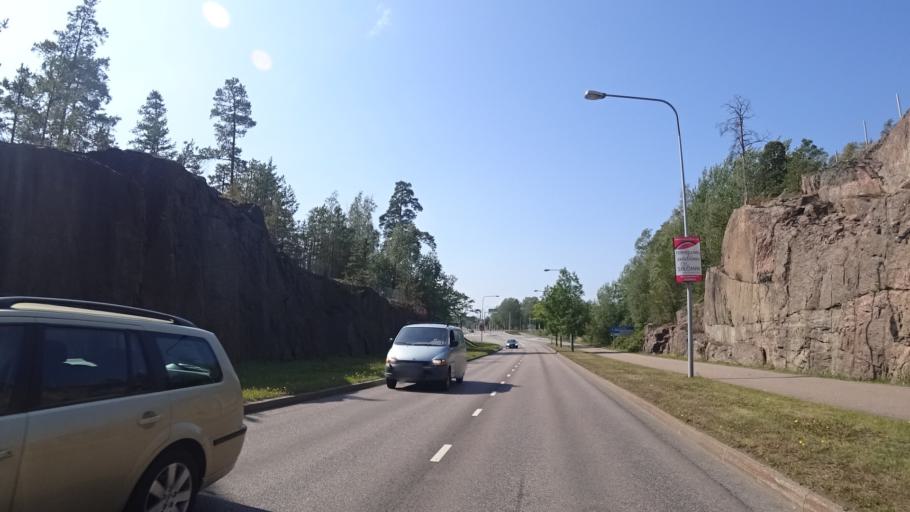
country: FI
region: Kymenlaakso
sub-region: Kotka-Hamina
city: Karhula
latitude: 60.5092
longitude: 26.9257
